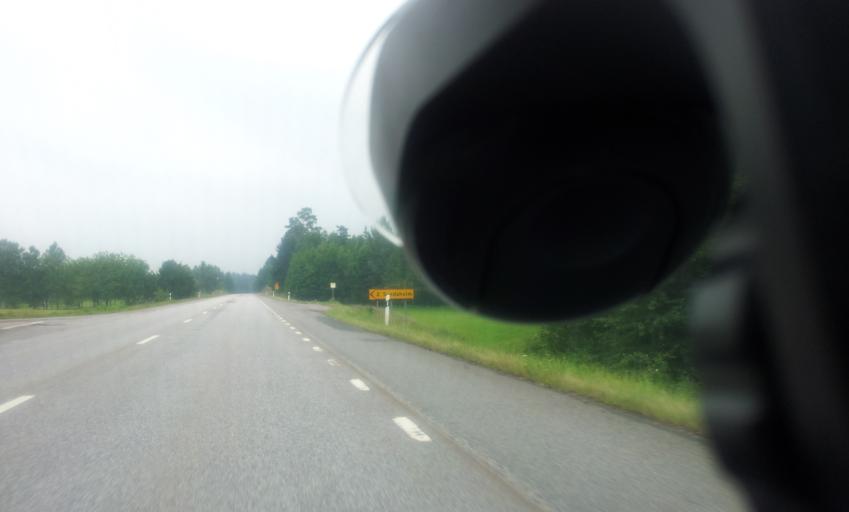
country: SE
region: Kalmar
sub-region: Vasterviks Kommun
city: Ankarsrum
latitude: 57.6868
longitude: 16.4409
